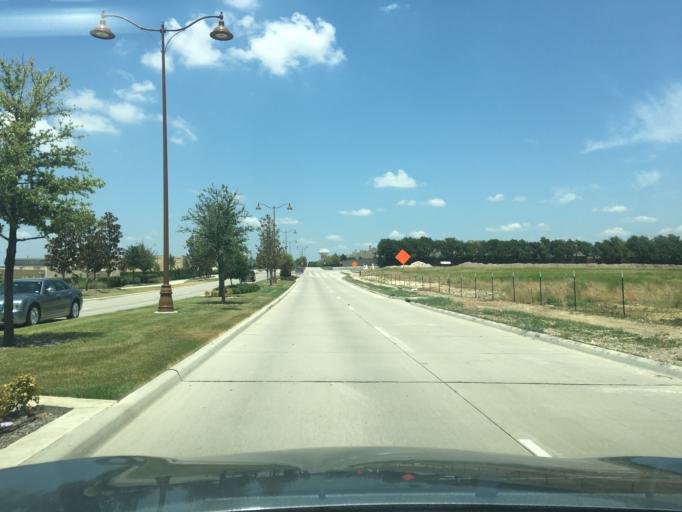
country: US
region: Texas
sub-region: Collin County
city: Prosper
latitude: 33.2200
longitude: -96.7938
